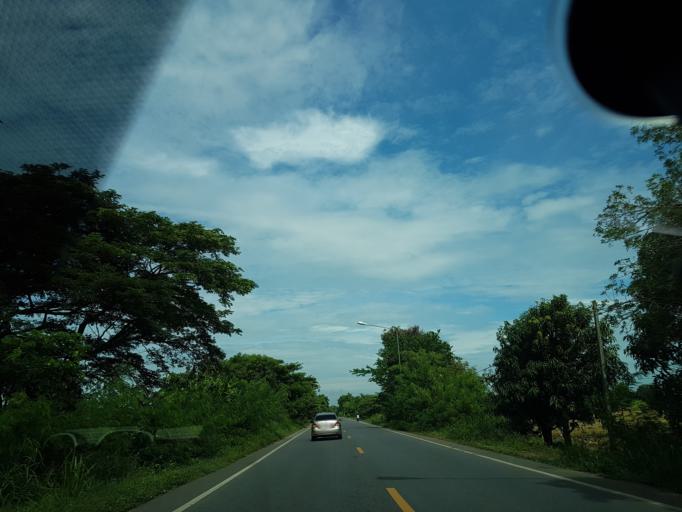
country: TH
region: Ang Thong
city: Chaiyo
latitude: 14.7228
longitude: 100.4710
